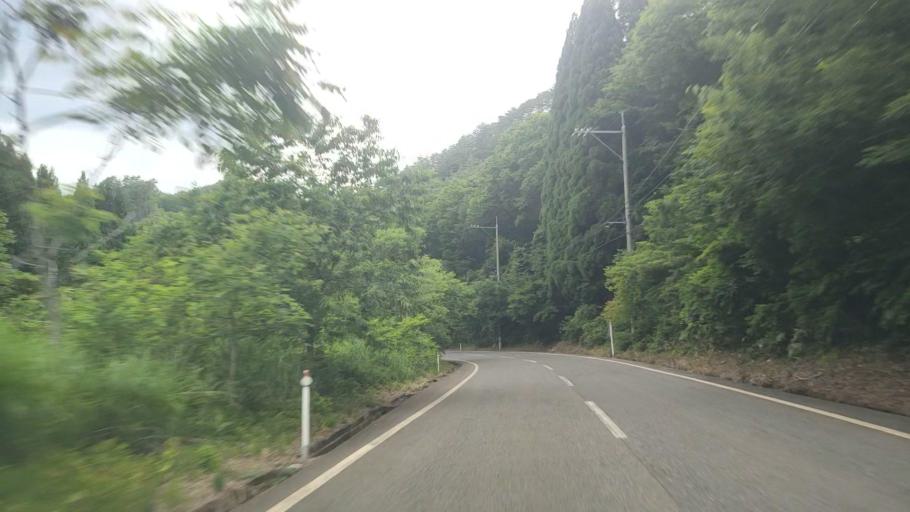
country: JP
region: Tottori
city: Kurayoshi
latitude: 35.2947
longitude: 133.9846
